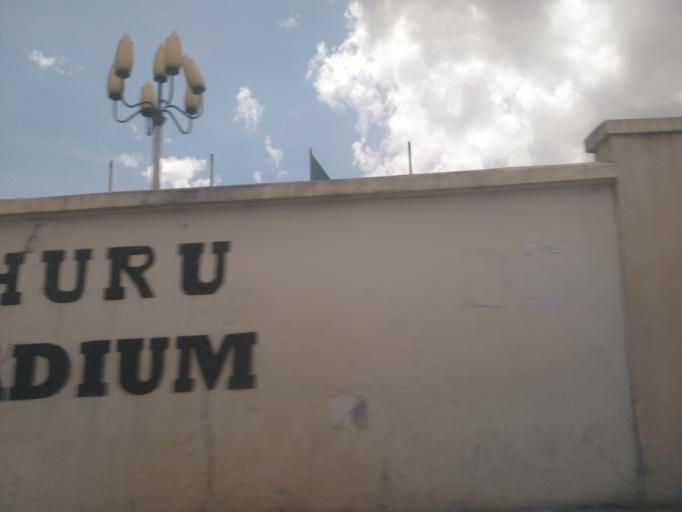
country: TZ
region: Dar es Salaam
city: Dar es Salaam
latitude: -6.8557
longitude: 39.2718
